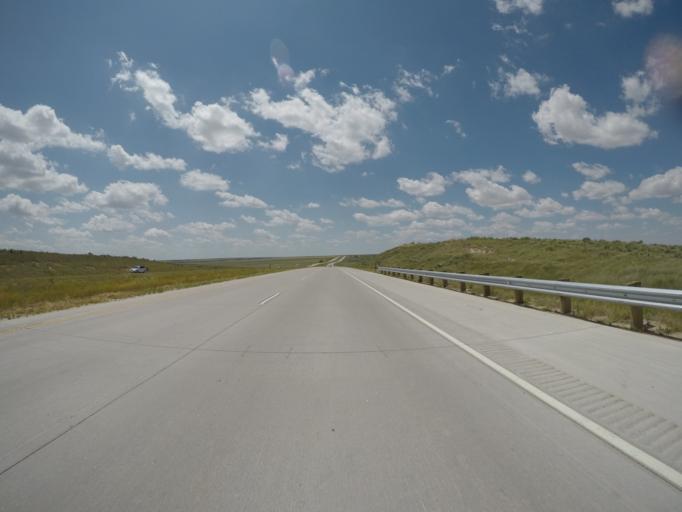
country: US
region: Colorado
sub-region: Kit Carson County
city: Burlington
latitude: 39.2941
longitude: -102.6413
